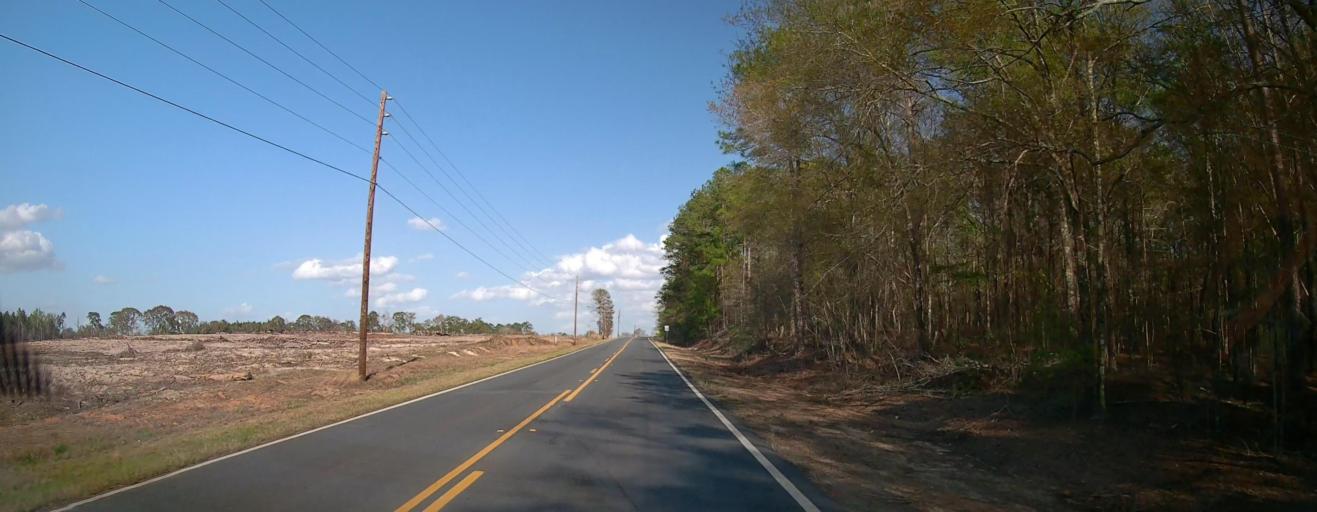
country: US
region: Georgia
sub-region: Telfair County
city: McRae
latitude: 32.0439
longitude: -82.8270
